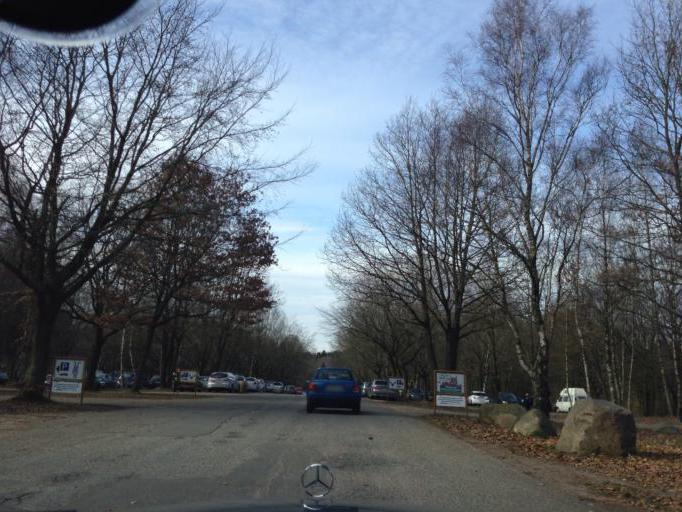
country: DE
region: Lower Saxony
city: Seevetal
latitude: 53.4412
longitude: 9.8899
